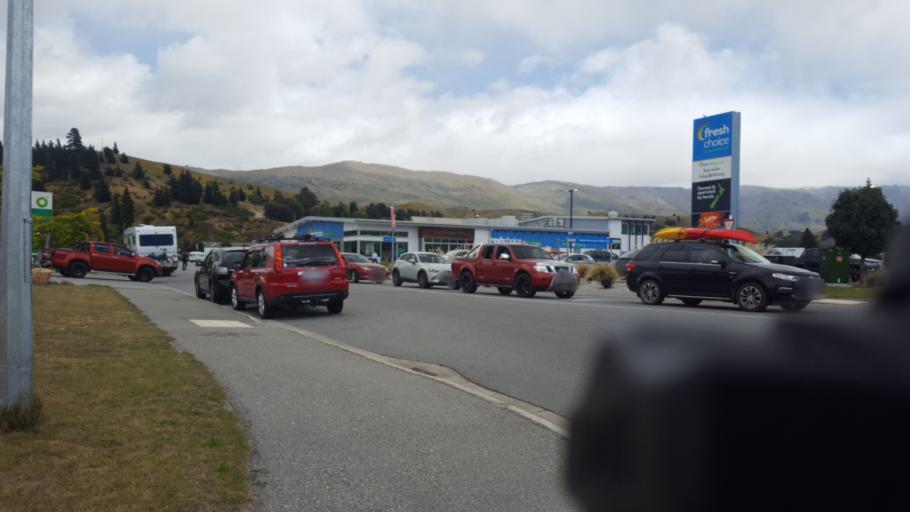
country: NZ
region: Otago
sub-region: Queenstown-Lakes District
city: Wanaka
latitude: -45.0361
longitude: 169.1944
